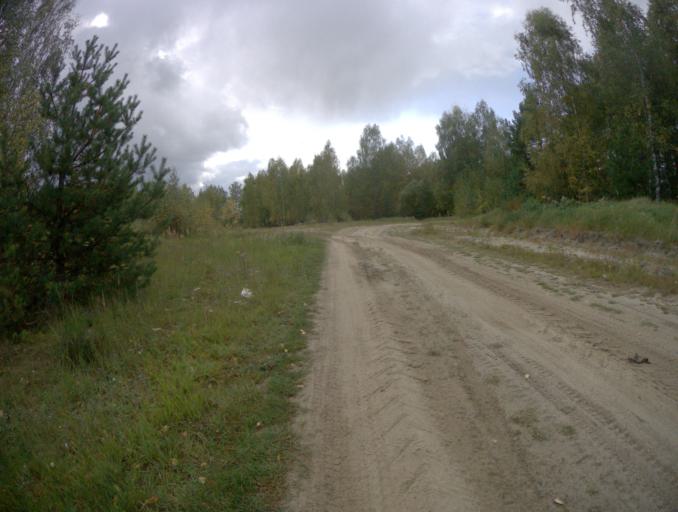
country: RU
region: Vladimir
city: Urshel'skiy
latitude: 55.8115
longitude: 40.1564
